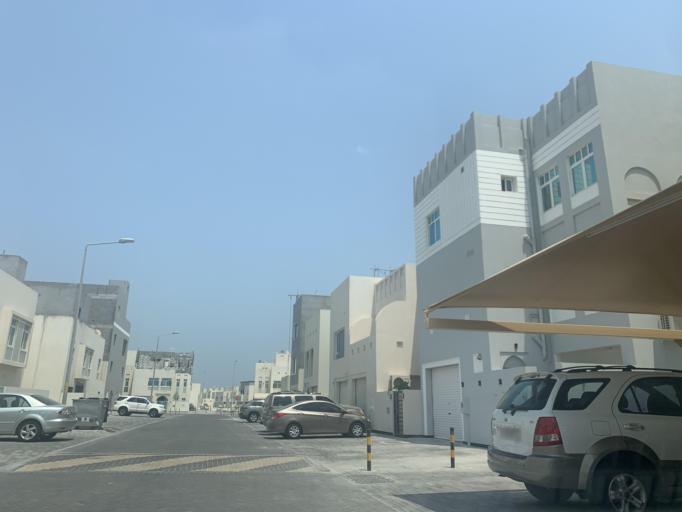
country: BH
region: Muharraq
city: Al Hadd
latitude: 26.2321
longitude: 50.6607
